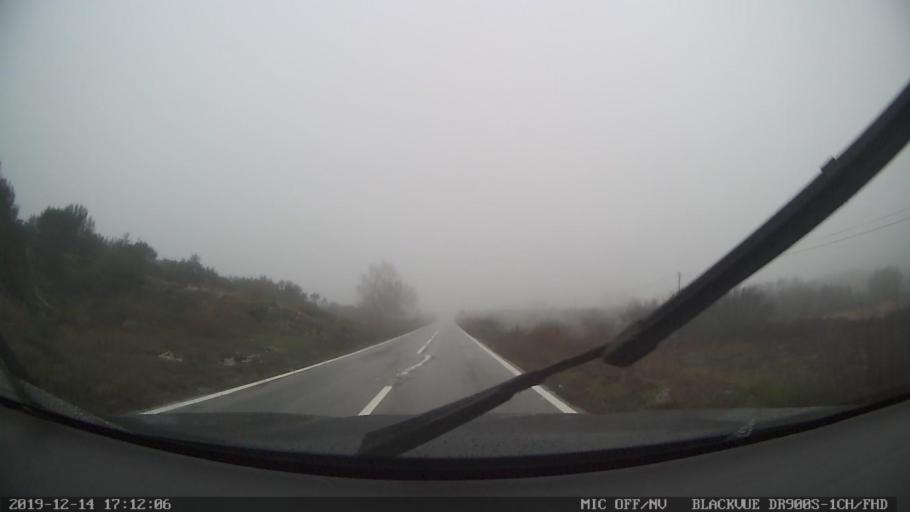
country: PT
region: Vila Real
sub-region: Vila Pouca de Aguiar
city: Vila Pouca de Aguiar
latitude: 41.4907
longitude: -7.6200
